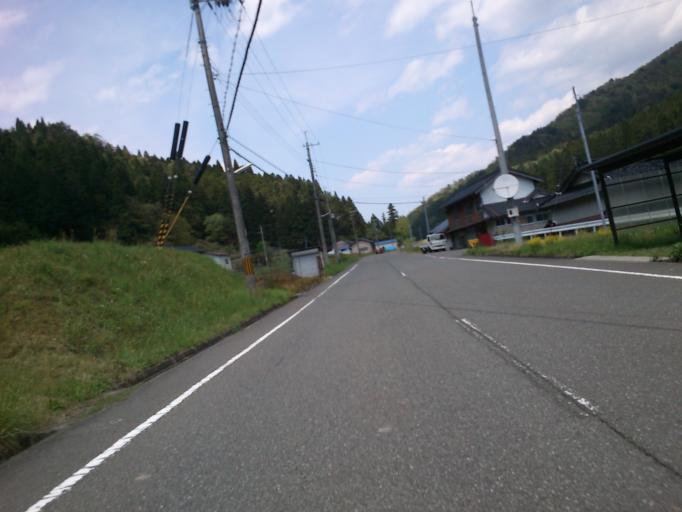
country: JP
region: Kyoto
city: Fukuchiyama
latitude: 35.3780
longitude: 134.9381
